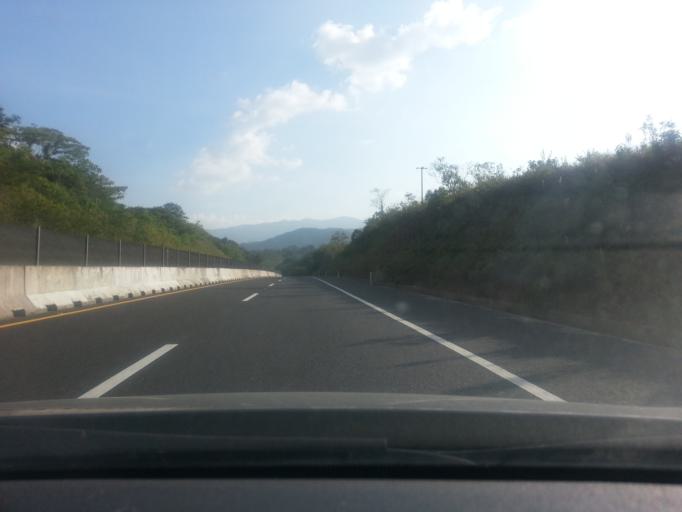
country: MX
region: Puebla
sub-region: Xicotepec
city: San Lorenzo
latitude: 20.4084
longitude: -97.9375
